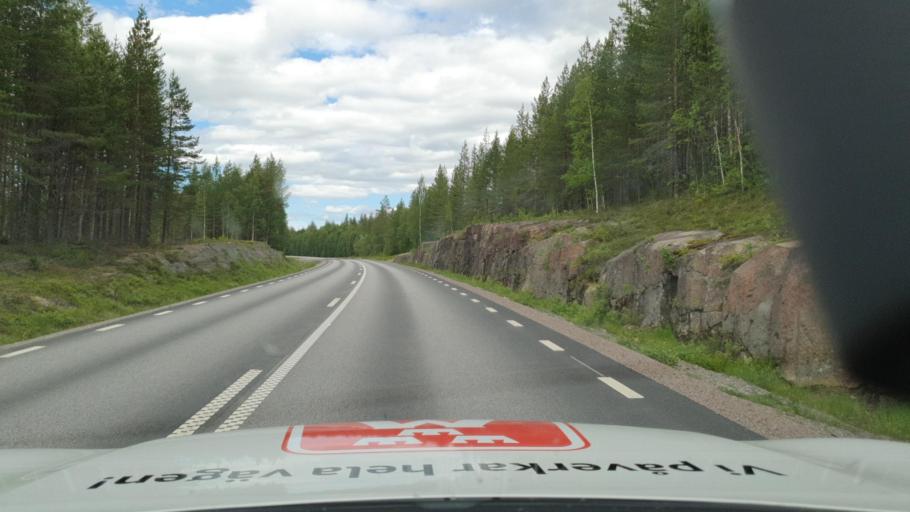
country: SE
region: Vaesterbotten
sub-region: Norsjo Kommun
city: Norsjoe
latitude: 65.1514
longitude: 19.8987
